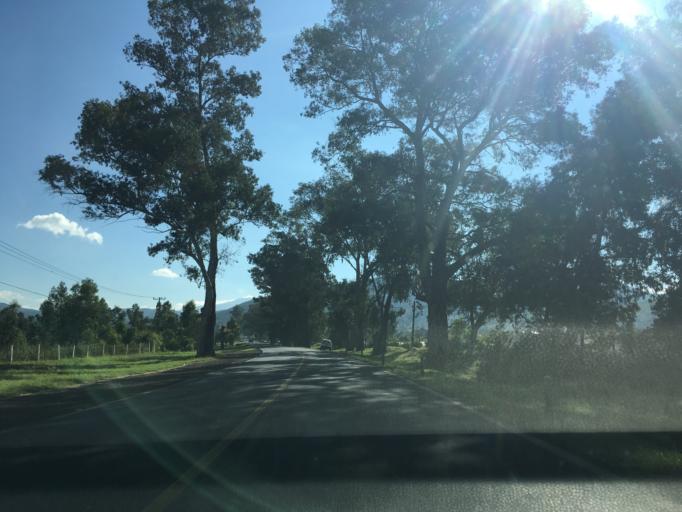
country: MX
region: Mexico
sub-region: Chalco
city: Santo Tomas
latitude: 19.8431
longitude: -102.0817
